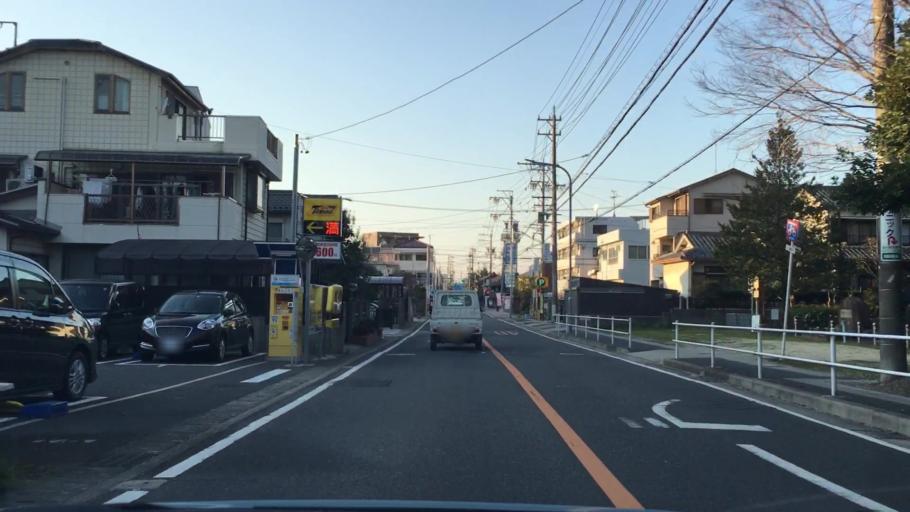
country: JP
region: Aichi
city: Obu
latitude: 35.0685
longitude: 136.9412
